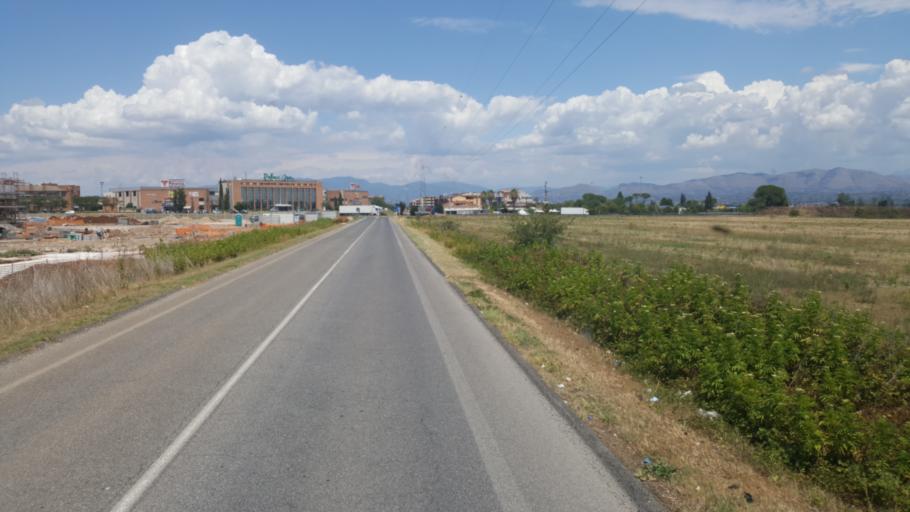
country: IT
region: Latium
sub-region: Citta metropolitana di Roma Capitale
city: Bivio di Capanelle
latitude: 42.1373
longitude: 12.5985
